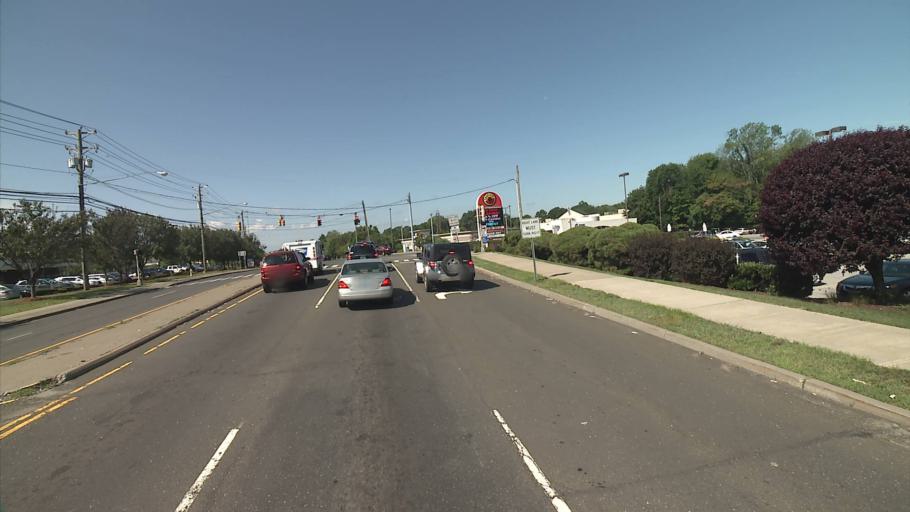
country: US
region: Connecticut
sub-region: Fairfield County
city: Norwalk
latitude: 41.1011
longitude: -73.4395
